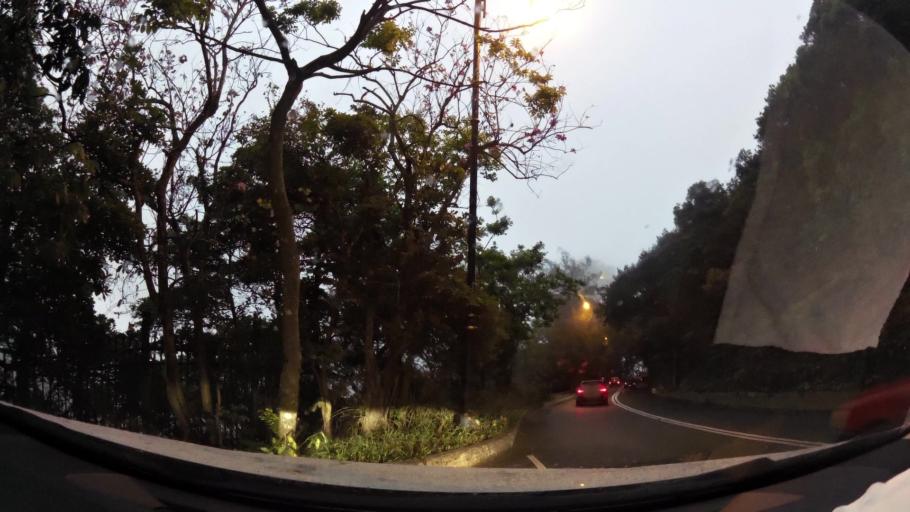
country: HK
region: Wanchai
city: Wan Chai
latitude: 22.2715
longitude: 114.1682
